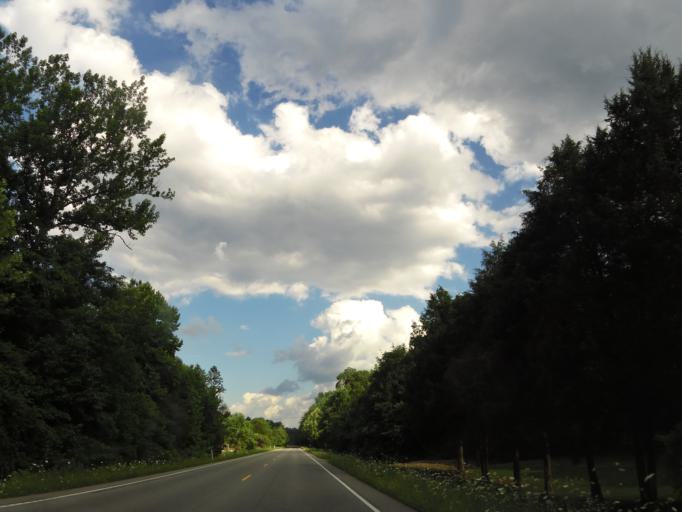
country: US
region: Tennessee
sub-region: Lewis County
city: Hohenwald
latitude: 35.5918
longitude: -87.6899
